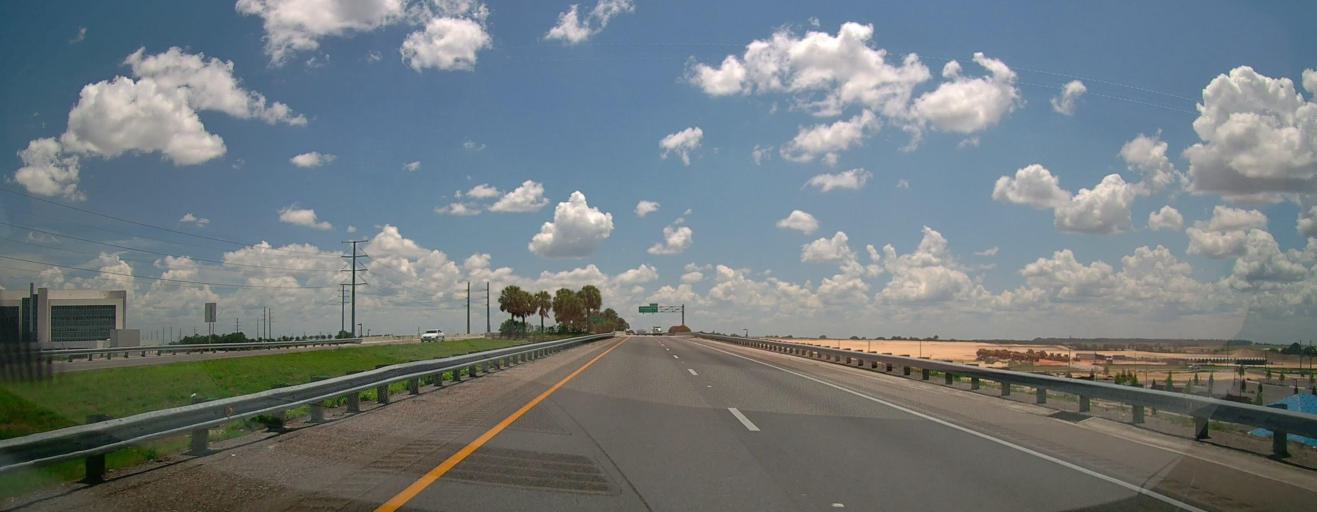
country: US
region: Florida
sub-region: Orange County
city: Oakland
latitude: 28.4613
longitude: -81.6338
